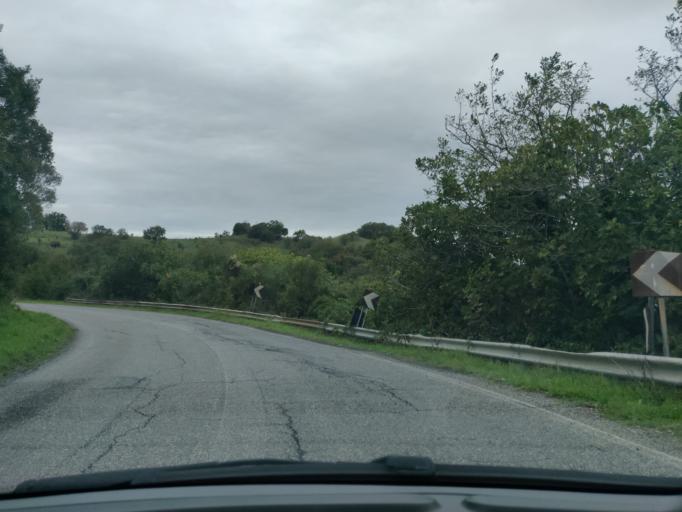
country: IT
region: Latium
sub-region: Citta metropolitana di Roma Capitale
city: Allumiere
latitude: 42.1450
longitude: 11.8839
